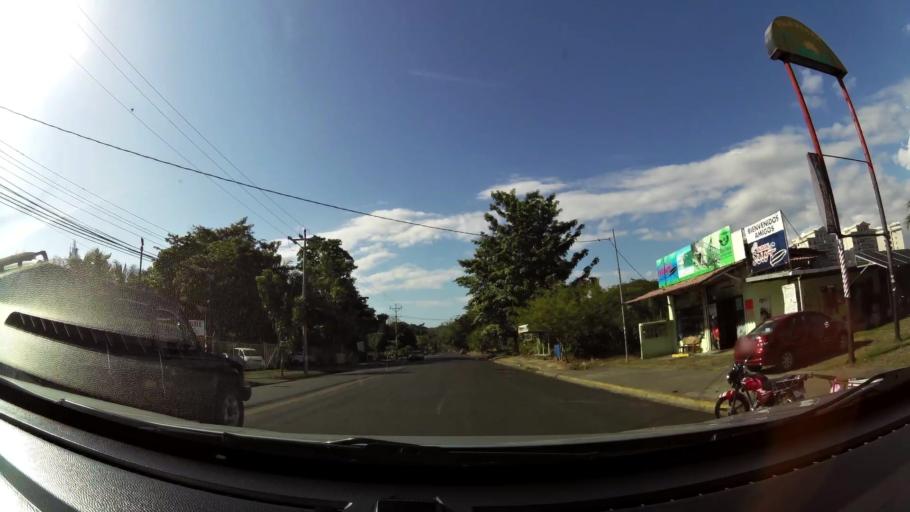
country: CR
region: Puntarenas
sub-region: Canton de Garabito
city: Jaco
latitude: 9.6188
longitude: -84.6331
